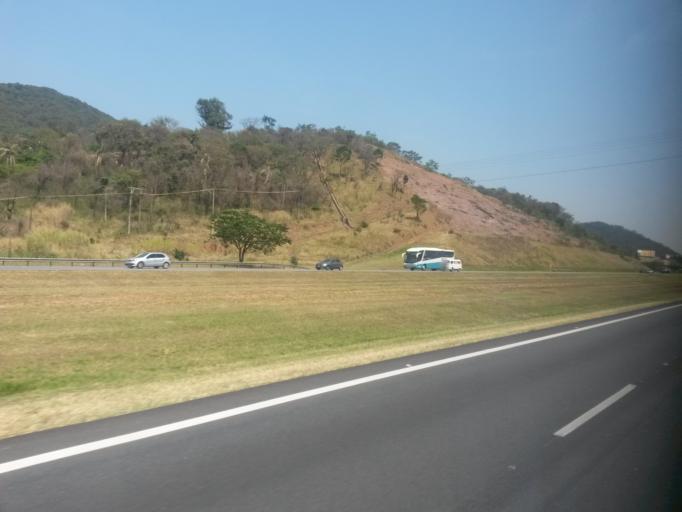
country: BR
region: Sao Paulo
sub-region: Jundiai
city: Jundiai
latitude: -23.2357
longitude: -46.8905
